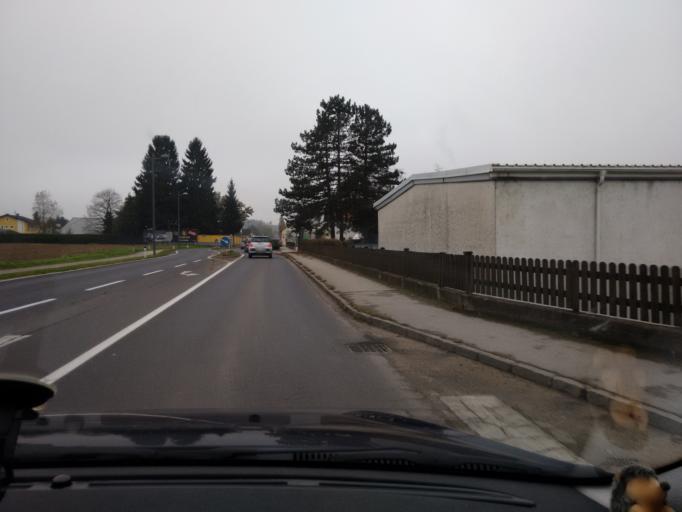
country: AT
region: Upper Austria
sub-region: Wels-Land
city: Sattledt
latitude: 48.0728
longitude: 14.0633
